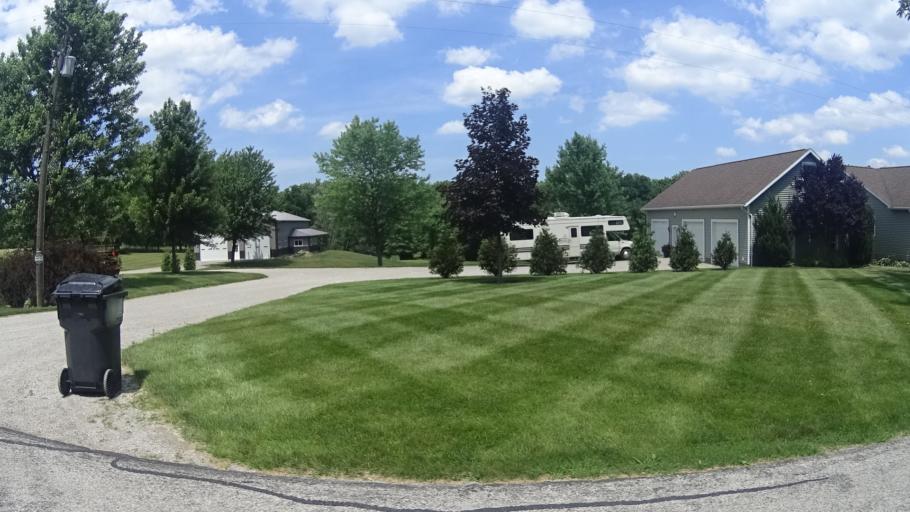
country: US
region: Ohio
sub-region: Erie County
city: Milan
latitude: 41.3196
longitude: -82.5298
